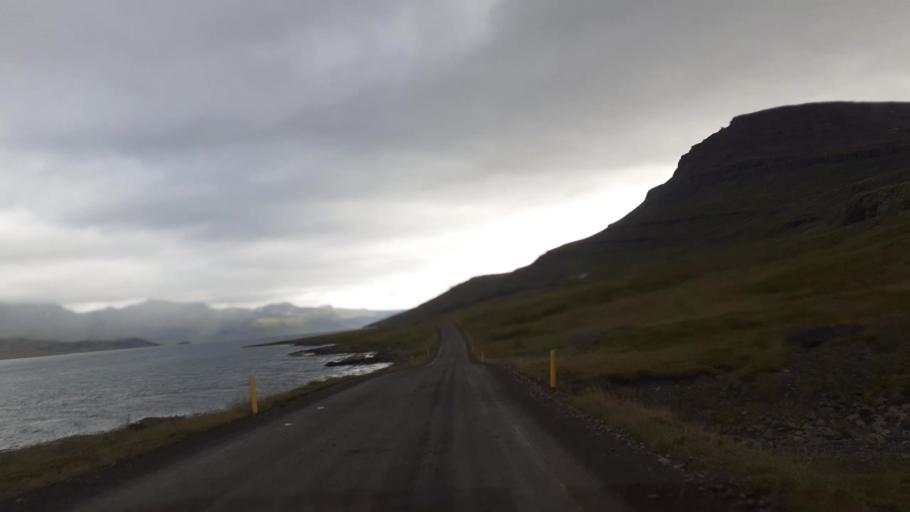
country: IS
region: East
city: Reydarfjoerdur
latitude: 65.0130
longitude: -14.1622
